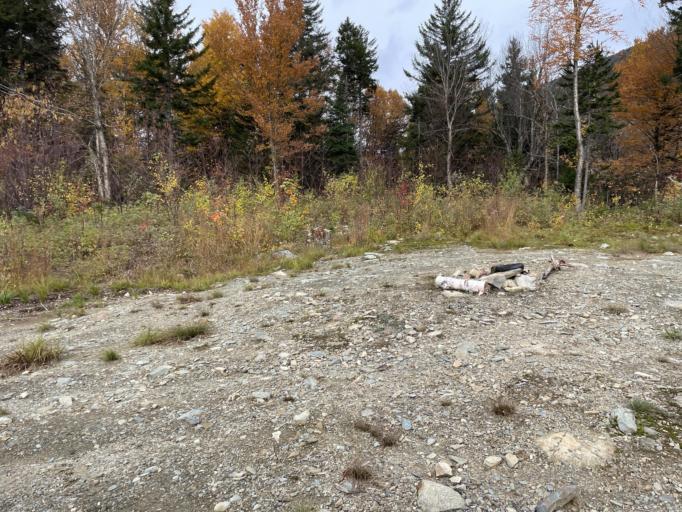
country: CA
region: Quebec
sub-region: Estrie
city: Lac-Megantic
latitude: 45.3249
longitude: -71.0091
